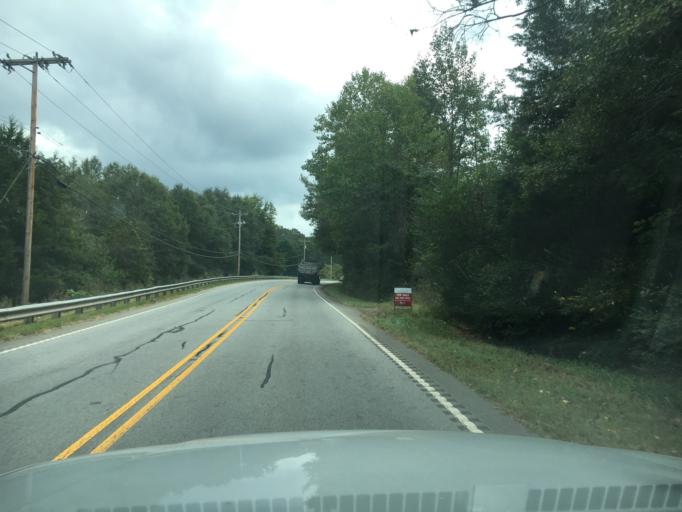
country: US
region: South Carolina
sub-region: Greenville County
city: Greer
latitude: 34.9768
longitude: -82.2429
